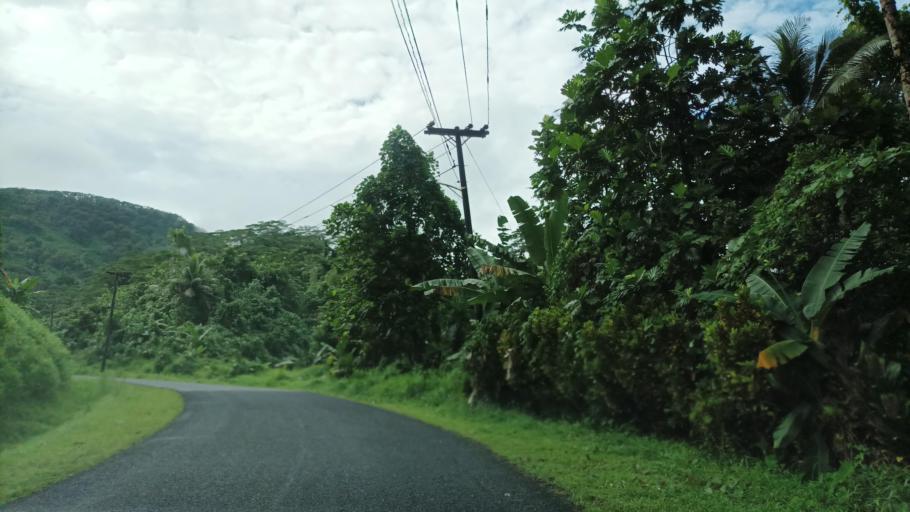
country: FM
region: Pohnpei
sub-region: Sokehs Municipality
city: Palikir - National Government Center
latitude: 6.9281
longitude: 158.1757
